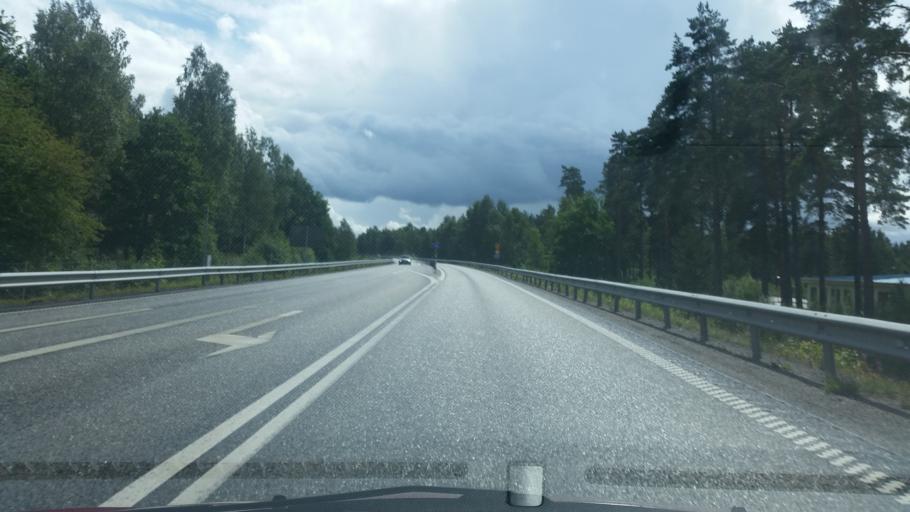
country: SE
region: Joenkoeping
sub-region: Gislaveds Kommun
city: Gislaved
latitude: 57.2747
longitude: 13.6166
